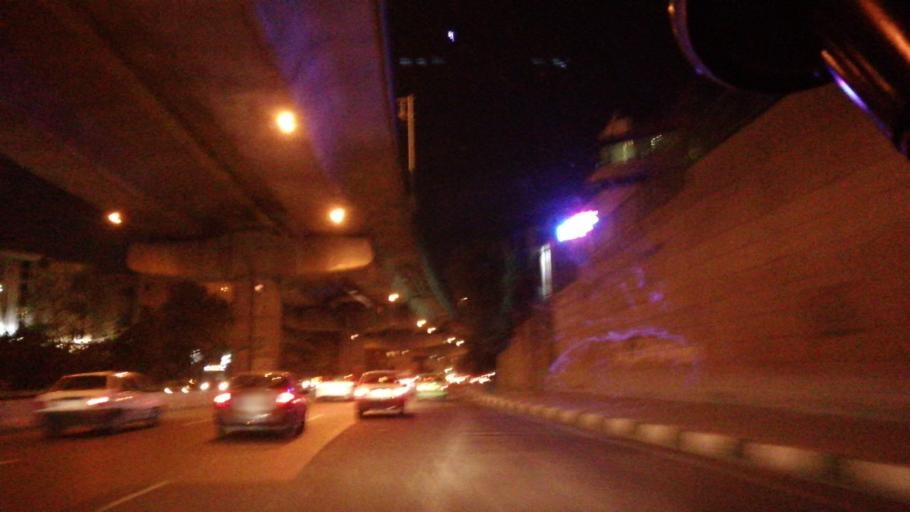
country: IR
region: Tehran
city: Tajrish
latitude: 35.7903
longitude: 51.4757
